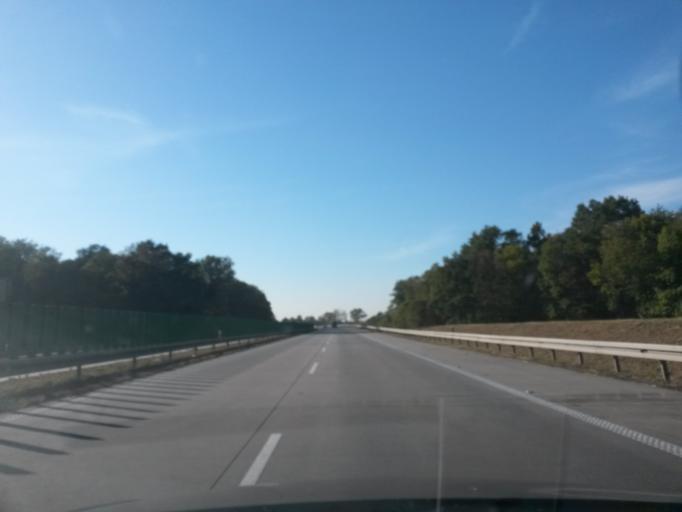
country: PL
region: Lower Silesian Voivodeship
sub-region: Powiat sredzki
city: Udanin
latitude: 51.0619
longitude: 16.5142
